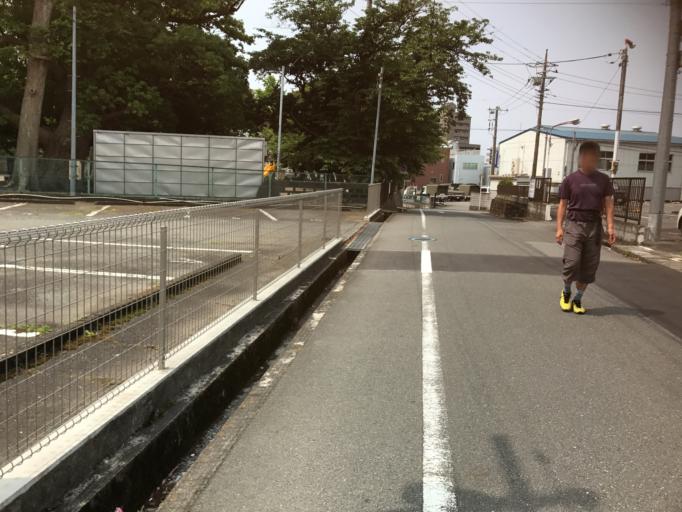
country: JP
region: Shizuoka
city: Numazu
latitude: 35.1014
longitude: 138.8684
